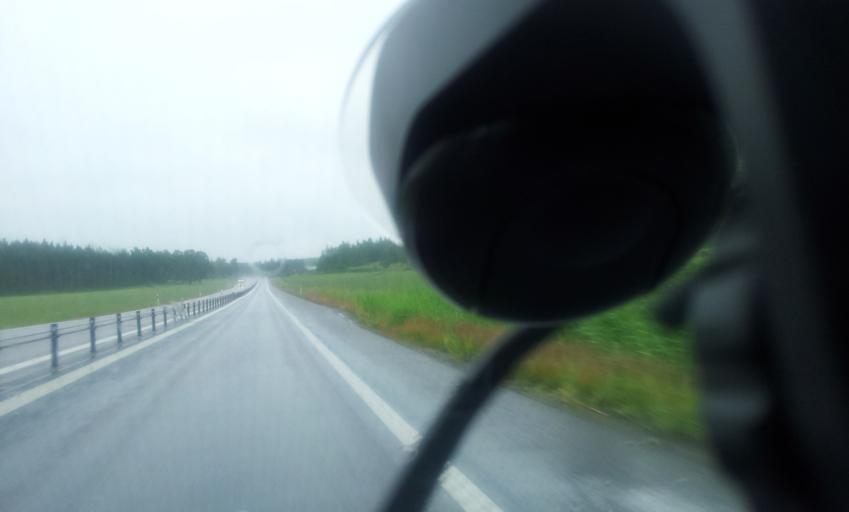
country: SE
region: OEstergoetland
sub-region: Soderkopings Kommun
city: Soederkoeping
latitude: 58.4039
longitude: 16.4024
